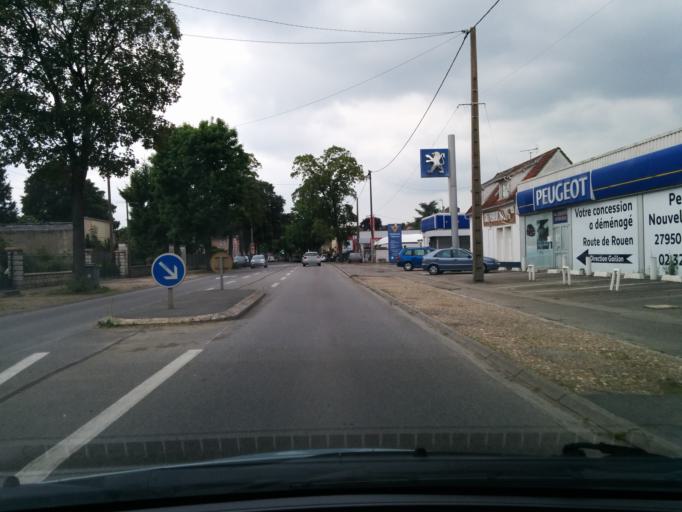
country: FR
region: Haute-Normandie
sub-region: Departement de l'Eure
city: Vernon
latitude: 49.0853
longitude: 1.4986
